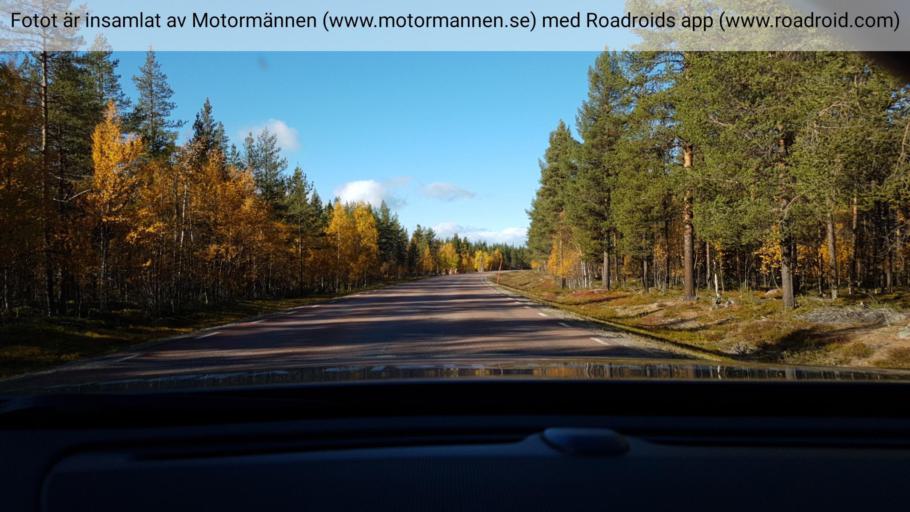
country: SE
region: Norrbotten
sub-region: Arjeplogs Kommun
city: Arjeplog
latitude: 66.0022
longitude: 18.1251
